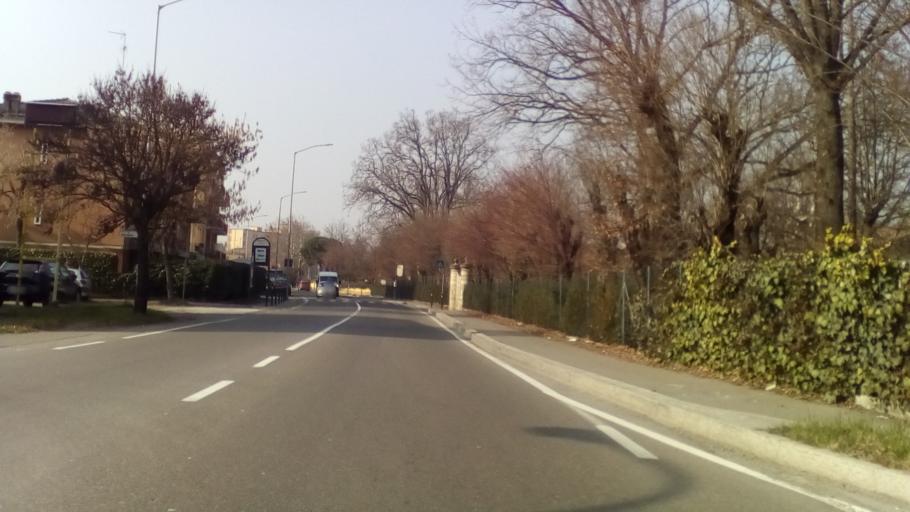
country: IT
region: Emilia-Romagna
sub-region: Provincia di Modena
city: Modena
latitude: 44.6274
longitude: 10.9474
